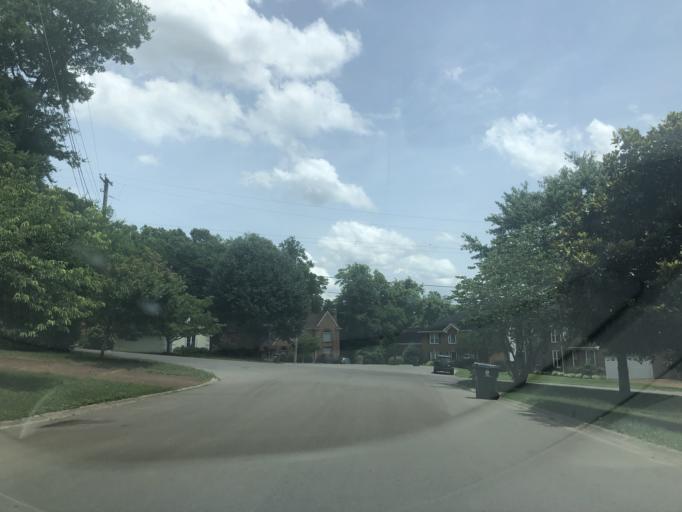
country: US
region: Tennessee
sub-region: Cheatham County
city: Pegram
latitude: 36.0475
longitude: -86.9601
